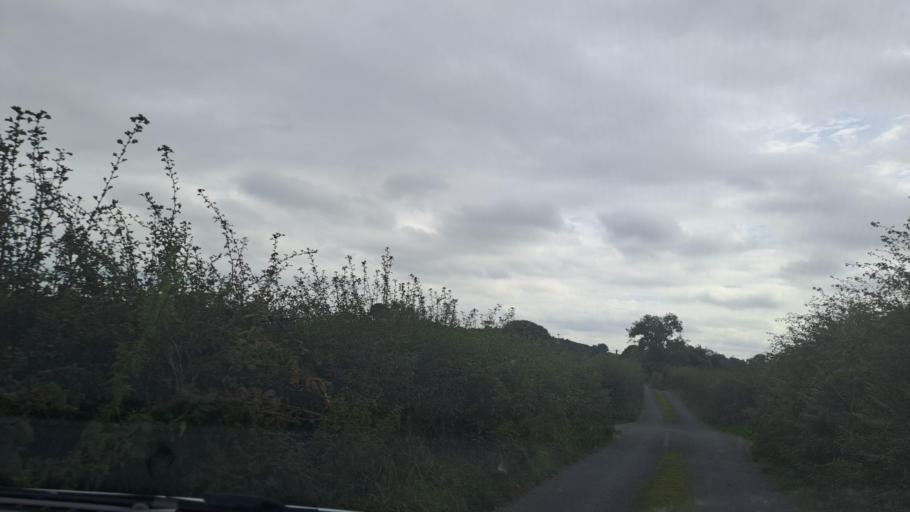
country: IE
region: Ulster
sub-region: An Cabhan
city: Kingscourt
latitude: 53.9742
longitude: -6.8509
